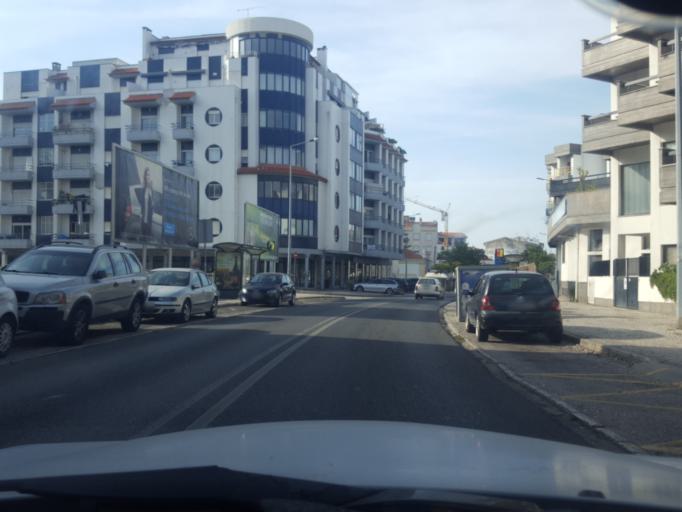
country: PT
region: Leiria
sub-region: Leiria
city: Leiria
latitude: 39.7391
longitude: -8.8025
